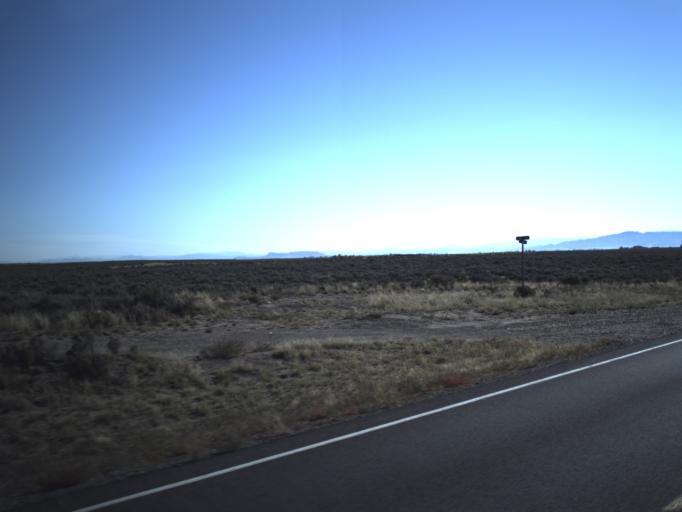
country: US
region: Utah
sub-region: Washington County
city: Enterprise
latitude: 37.7753
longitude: -113.8434
